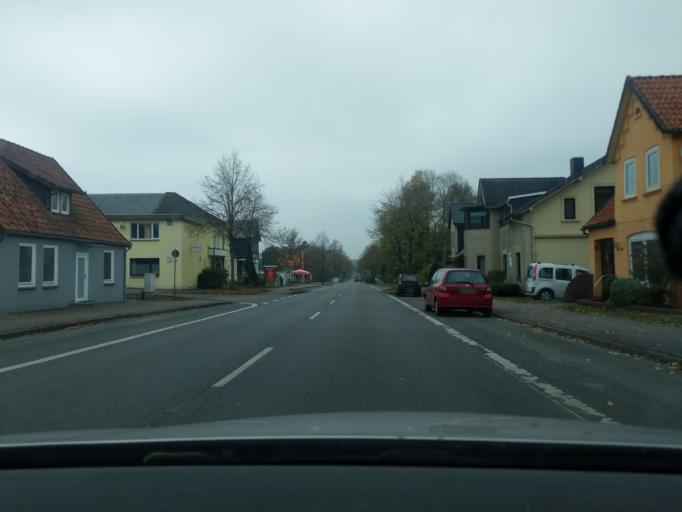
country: DE
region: Lower Saxony
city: Hemmoor
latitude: 53.7020
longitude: 9.1351
